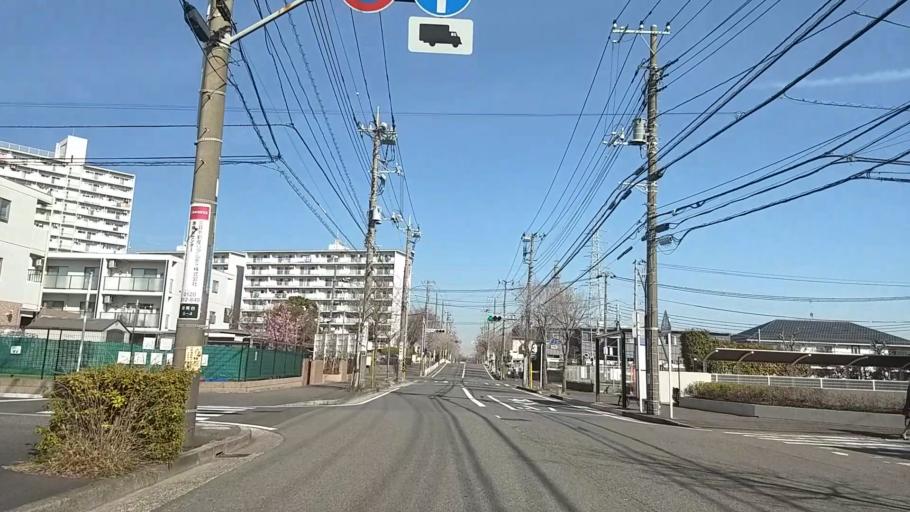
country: JP
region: Kanagawa
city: Kamakura
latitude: 35.3729
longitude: 139.5867
